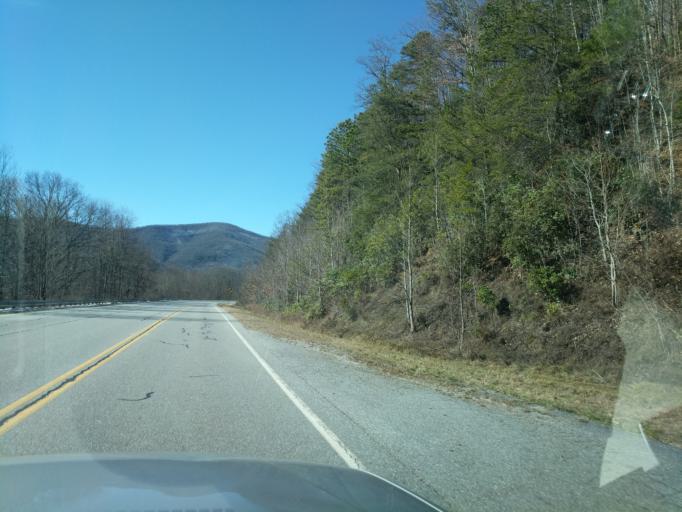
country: US
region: Georgia
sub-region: Towns County
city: Hiawassee
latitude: 34.8931
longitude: -83.5944
